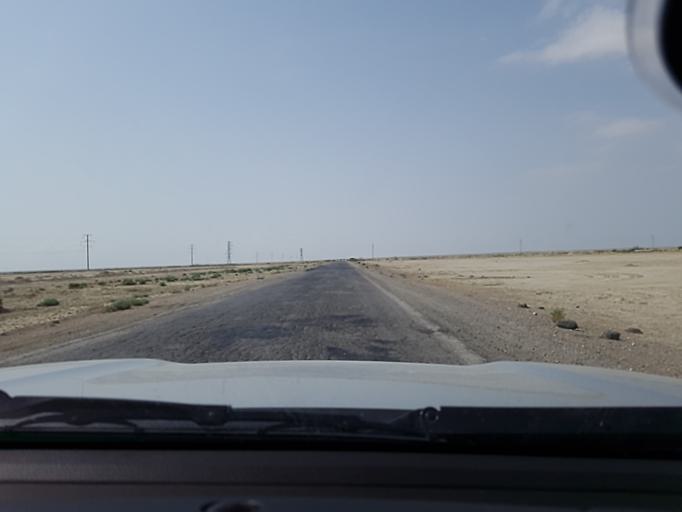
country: TM
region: Balkan
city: Gumdag
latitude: 39.0068
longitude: 54.5859
